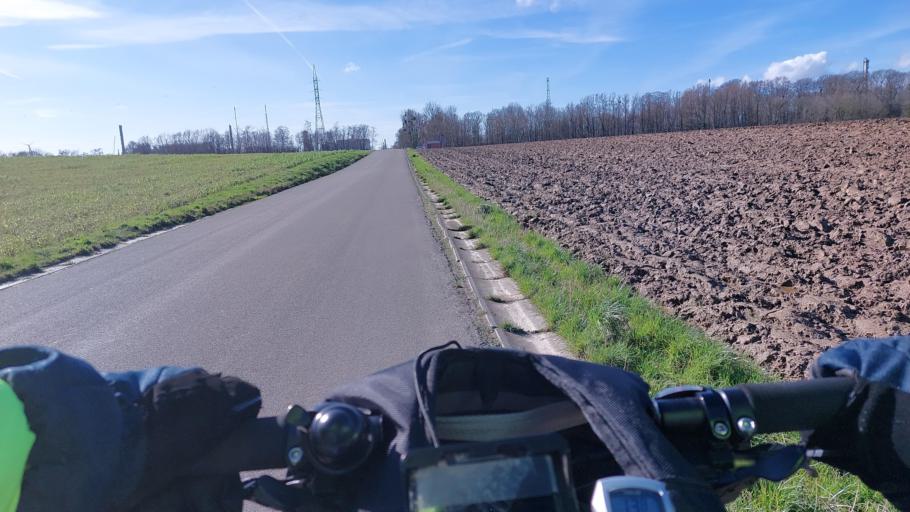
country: BE
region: Wallonia
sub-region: Province du Hainaut
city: Seneffe
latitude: 50.5587
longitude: 4.2298
